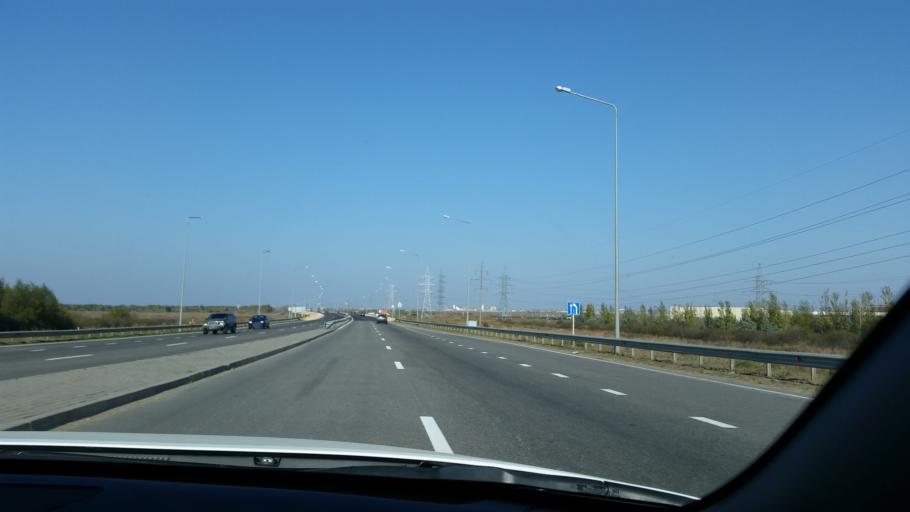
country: KZ
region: Astana Qalasy
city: Astana
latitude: 51.2056
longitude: 71.3116
